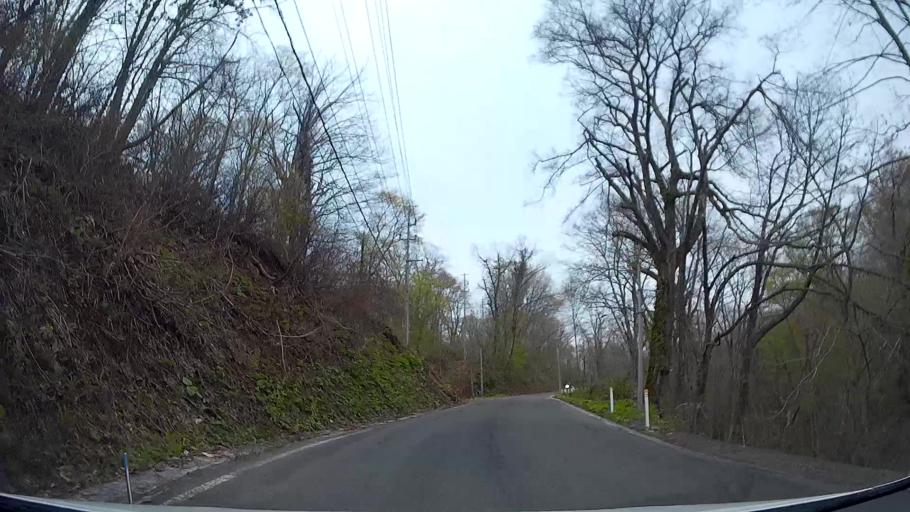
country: JP
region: Akita
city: Hanawa
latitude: 40.3960
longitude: 140.8719
